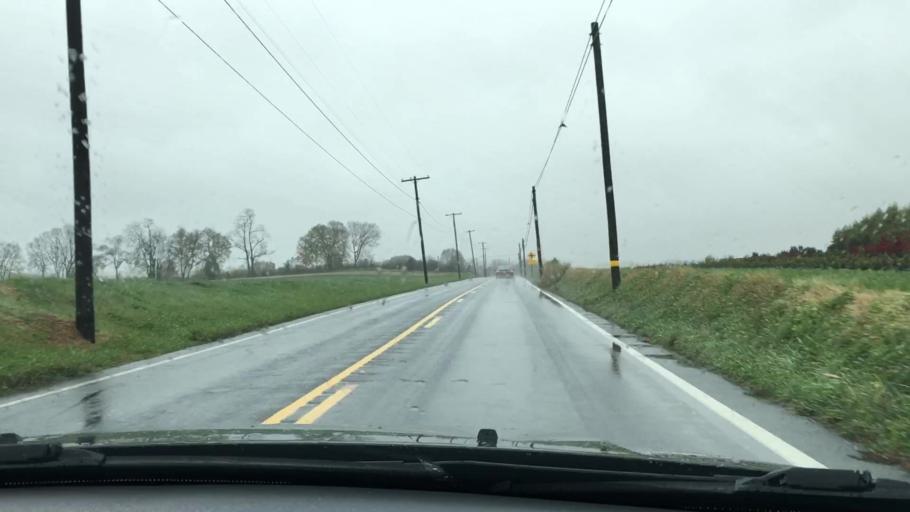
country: US
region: Maryland
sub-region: Frederick County
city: Adamstown
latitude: 39.2842
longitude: -77.4613
